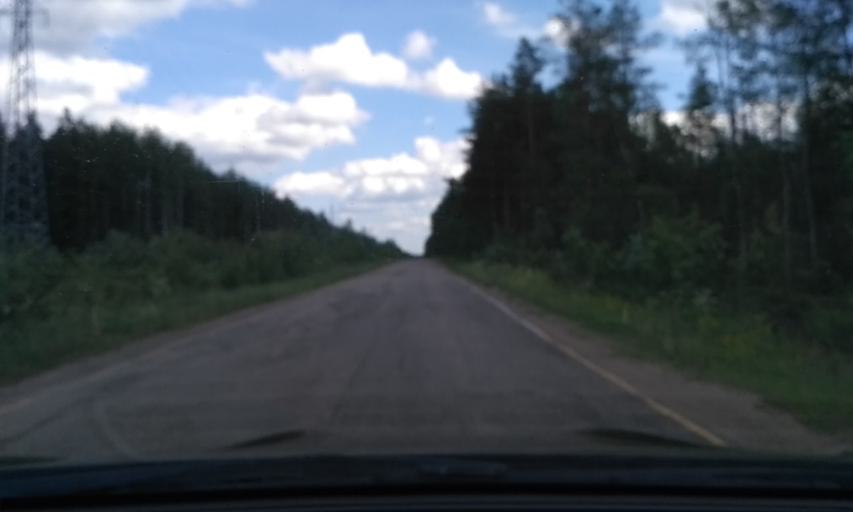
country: RU
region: Leningrad
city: Otradnoye
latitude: 59.8217
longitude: 30.7708
